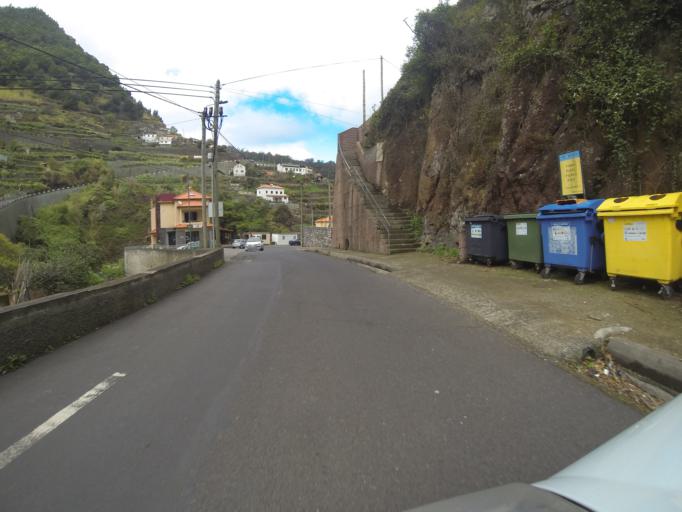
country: PT
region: Madeira
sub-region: Machico
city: Machico
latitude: 32.7347
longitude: -16.7893
